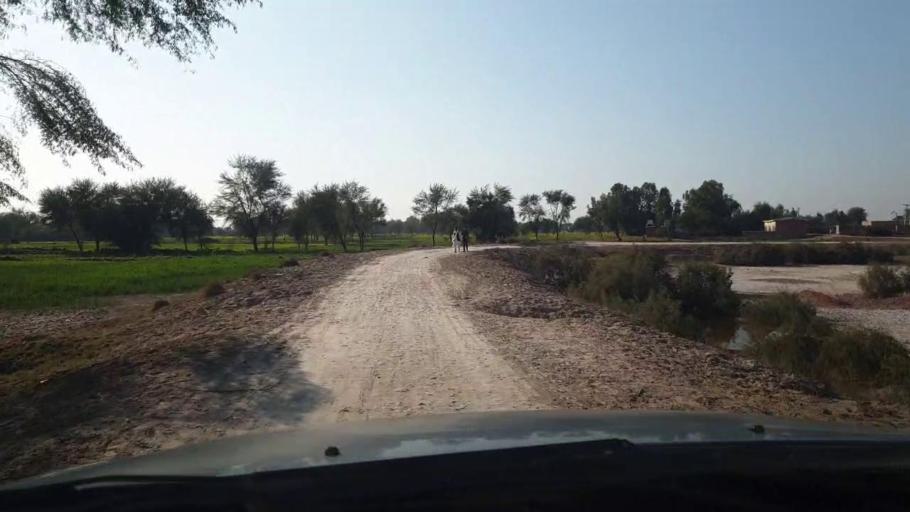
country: PK
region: Sindh
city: Mirpur Mathelo
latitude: 27.9823
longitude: 69.5322
